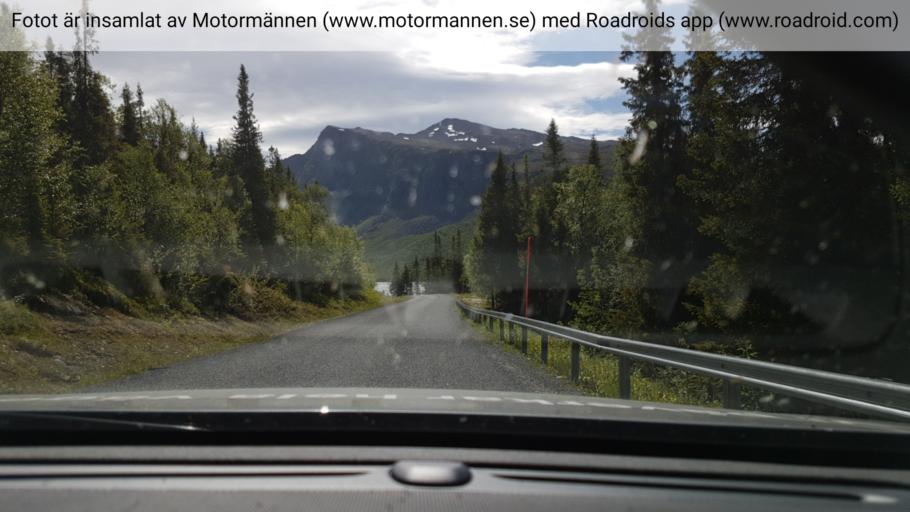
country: SE
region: Vaesterbotten
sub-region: Vilhelmina Kommun
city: Sjoberg
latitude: 65.2507
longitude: 15.4187
